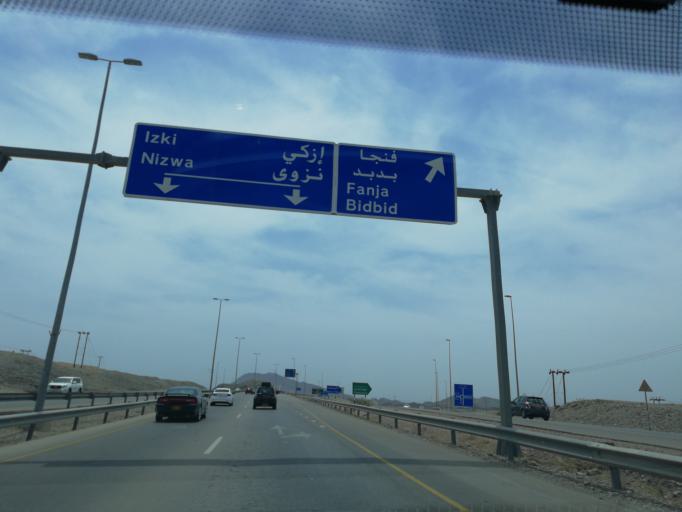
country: OM
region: Muhafazat ad Dakhiliyah
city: Bidbid
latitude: 23.4362
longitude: 58.1203
